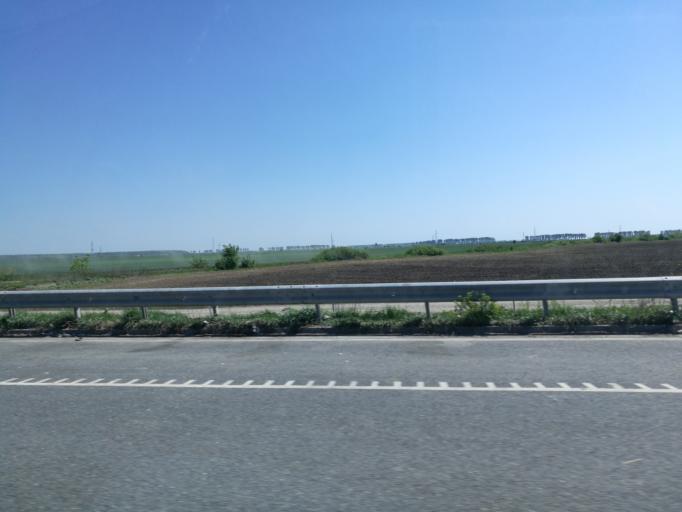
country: RO
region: Ilfov
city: Stefanestii de Jos
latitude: 44.5528
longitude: 26.1830
